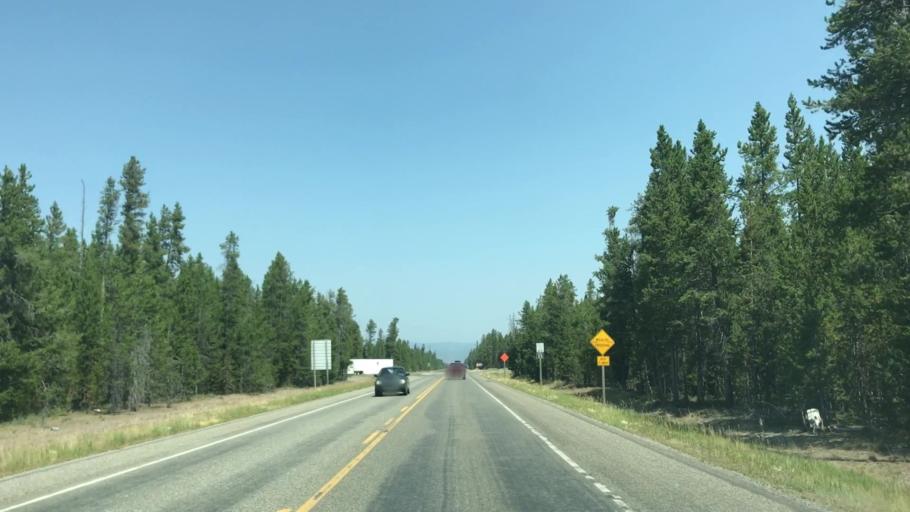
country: US
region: Montana
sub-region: Gallatin County
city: West Yellowstone
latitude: 44.6718
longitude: -111.1002
